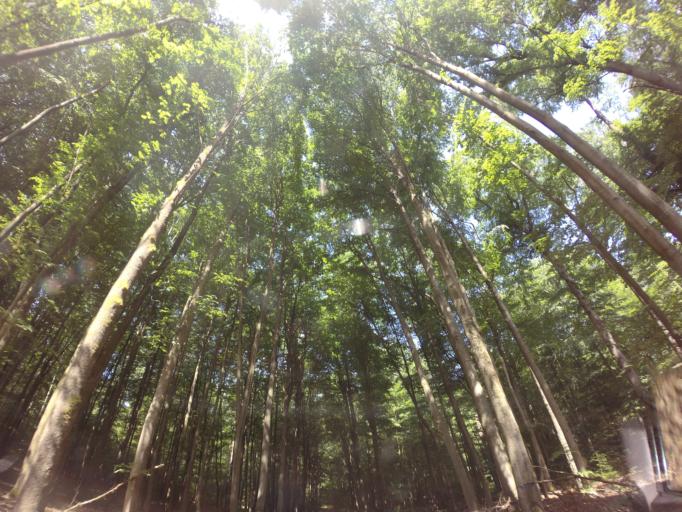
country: PL
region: West Pomeranian Voivodeship
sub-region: Powiat choszczenski
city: Drawno
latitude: 53.0978
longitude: 15.8936
